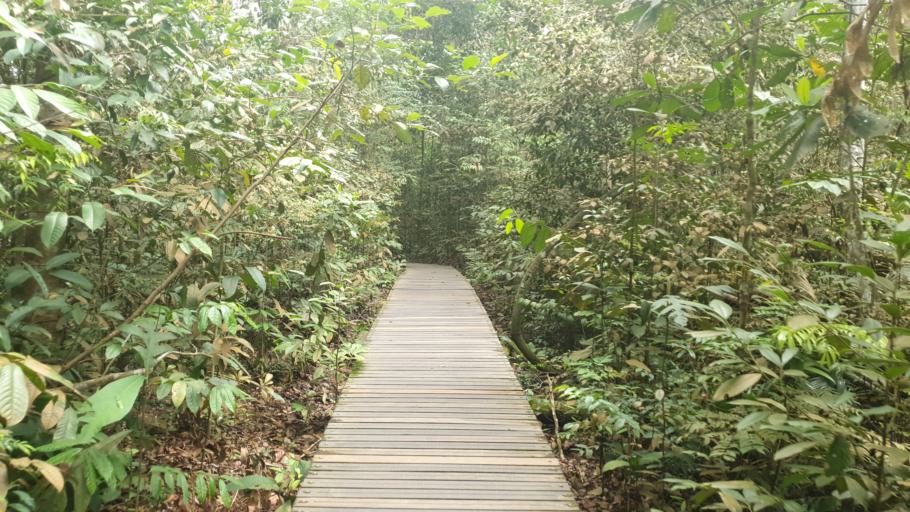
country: SG
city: Singapore
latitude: 1.3565
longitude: 103.8072
